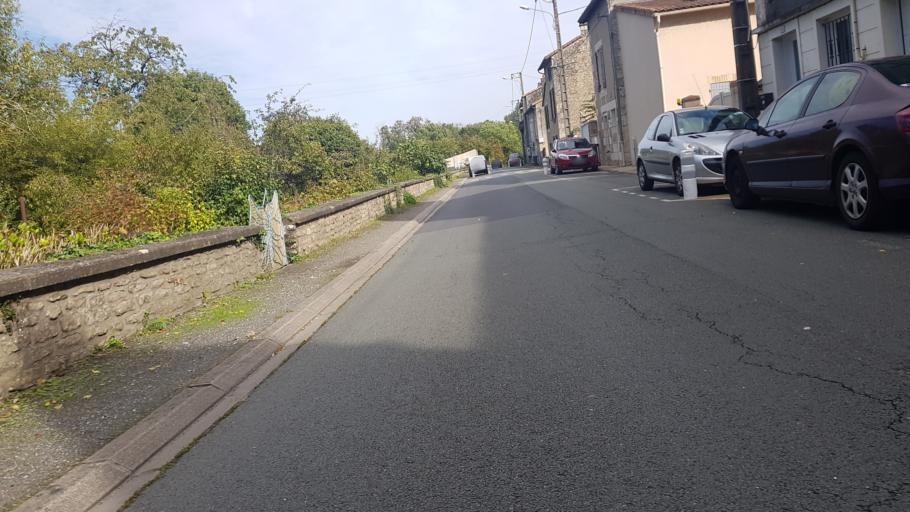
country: FR
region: Poitou-Charentes
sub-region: Departement de la Vienne
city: Chasseneuil-du-Poitou
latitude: 46.6182
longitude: 0.3595
